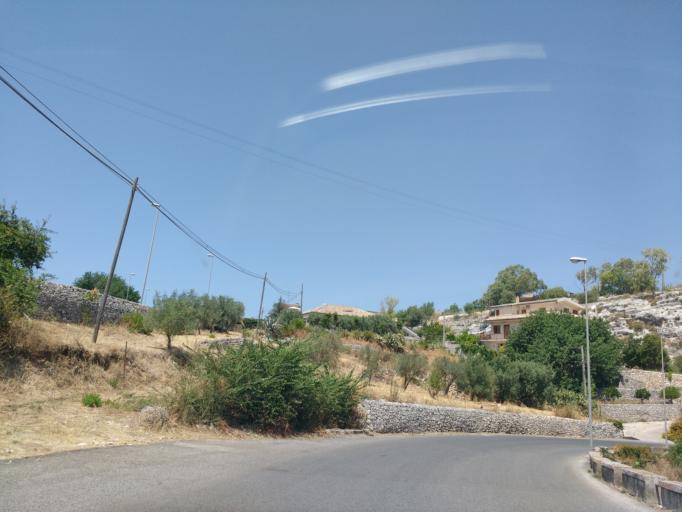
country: IT
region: Sicily
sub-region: Ragusa
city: Modica
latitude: 36.8668
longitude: 14.7503
